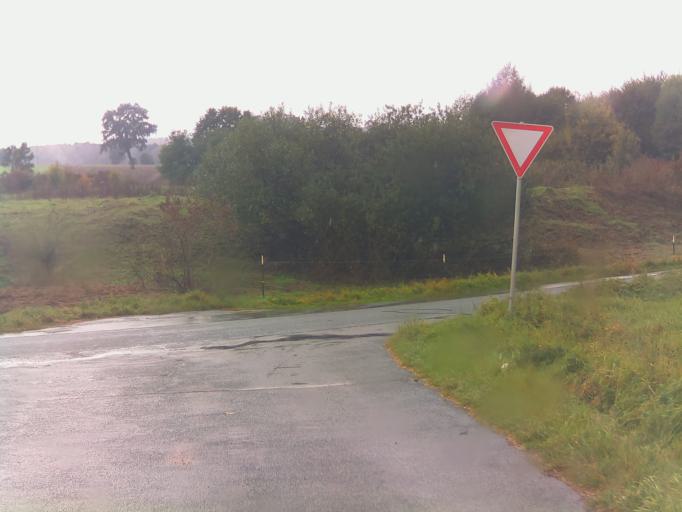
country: DE
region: Bavaria
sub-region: Upper Franconia
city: Kueps Oberfranken
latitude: 50.1738
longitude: 11.2924
